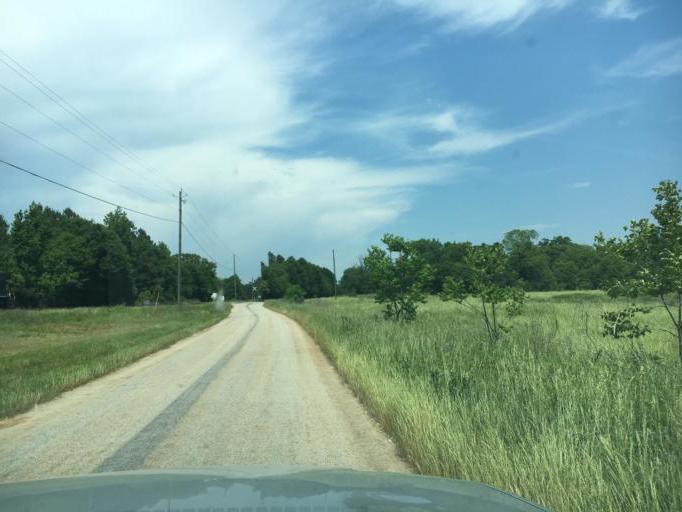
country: US
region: Georgia
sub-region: Franklin County
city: Lavonia
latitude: 34.3612
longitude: -83.0901
